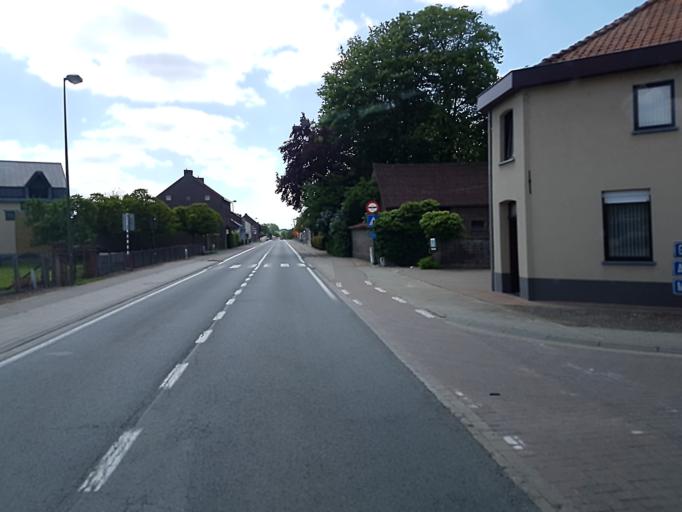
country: BE
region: Flanders
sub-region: Provincie Vlaams-Brabant
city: Glabbeek-Zuurbemde
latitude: 50.8682
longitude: 4.9587
